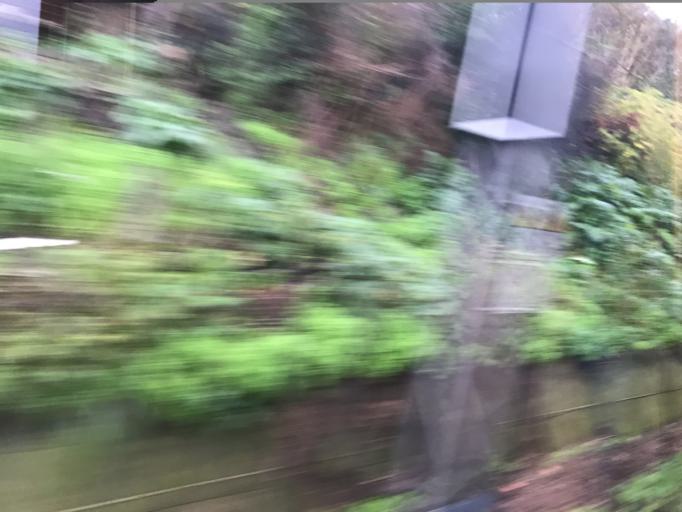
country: VA
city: Vatican City
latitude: 41.8608
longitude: 12.4621
